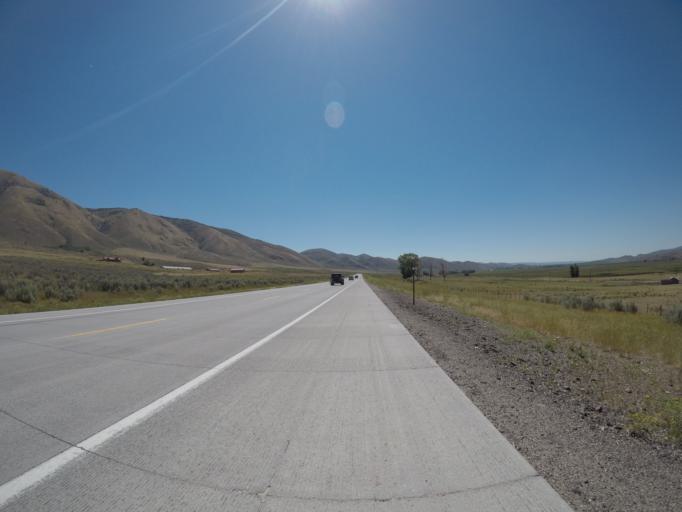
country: US
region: Idaho
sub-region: Bear Lake County
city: Montpelier
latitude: 42.1787
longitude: -111.0046
